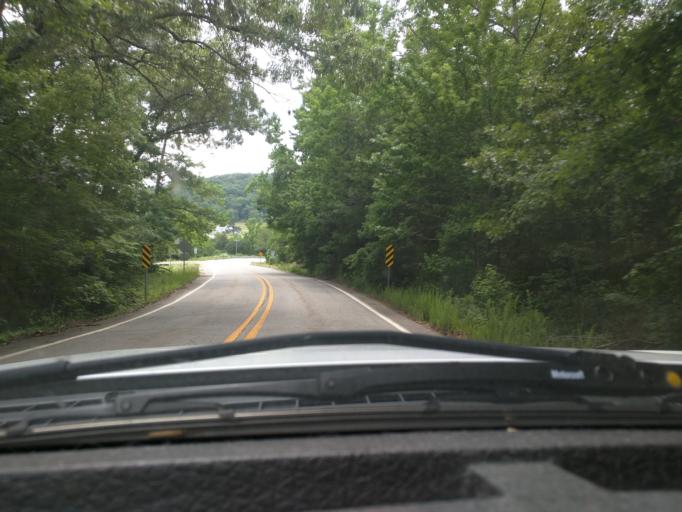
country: US
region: Arkansas
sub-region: Franklin County
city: Ozark
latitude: 35.6926
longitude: -93.8131
